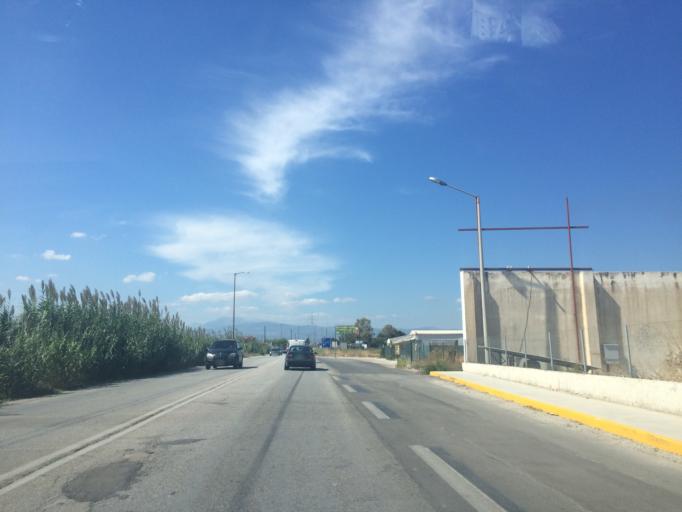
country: GR
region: Peloponnese
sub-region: Nomos Korinthias
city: Lekhaio
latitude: 37.9309
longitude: 22.8725
